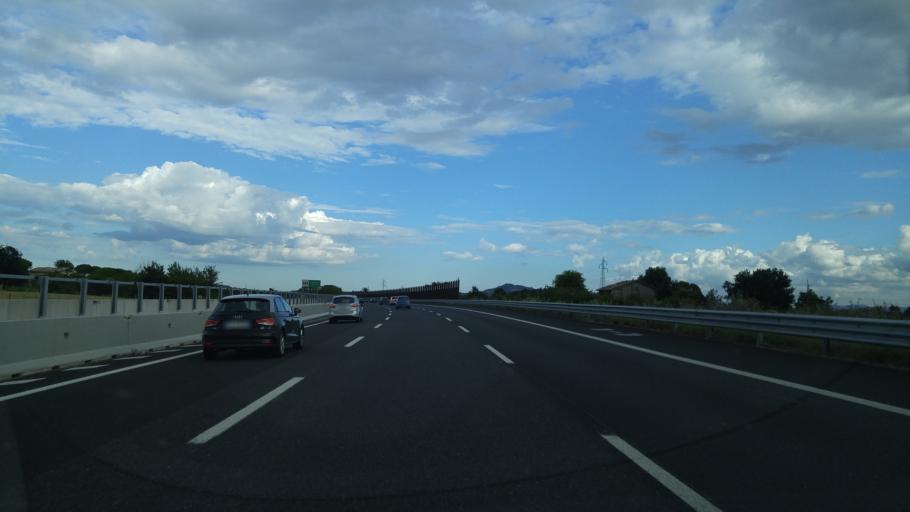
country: IT
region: Emilia-Romagna
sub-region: Provincia di Rimini
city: Montalbano
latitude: 43.9559
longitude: 12.7058
